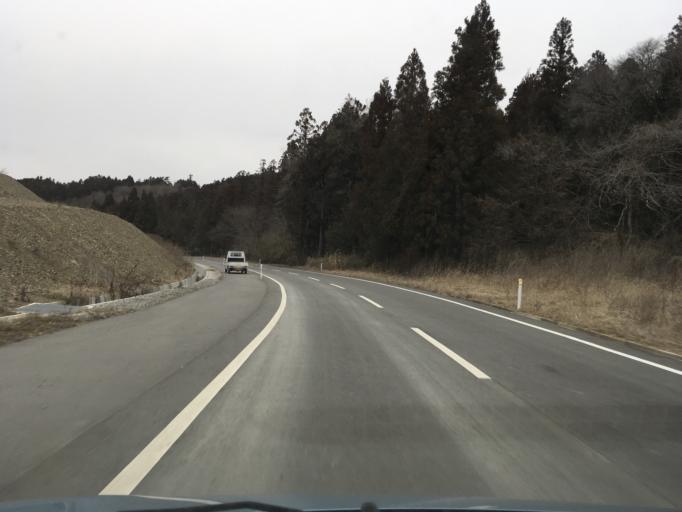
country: JP
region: Miyagi
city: Wakuya
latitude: 38.6688
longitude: 141.2774
